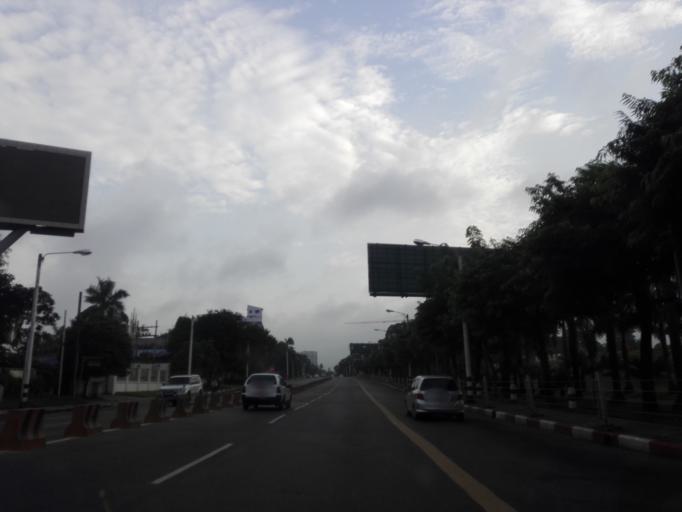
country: MM
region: Yangon
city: Yangon
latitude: 16.8397
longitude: 96.1348
